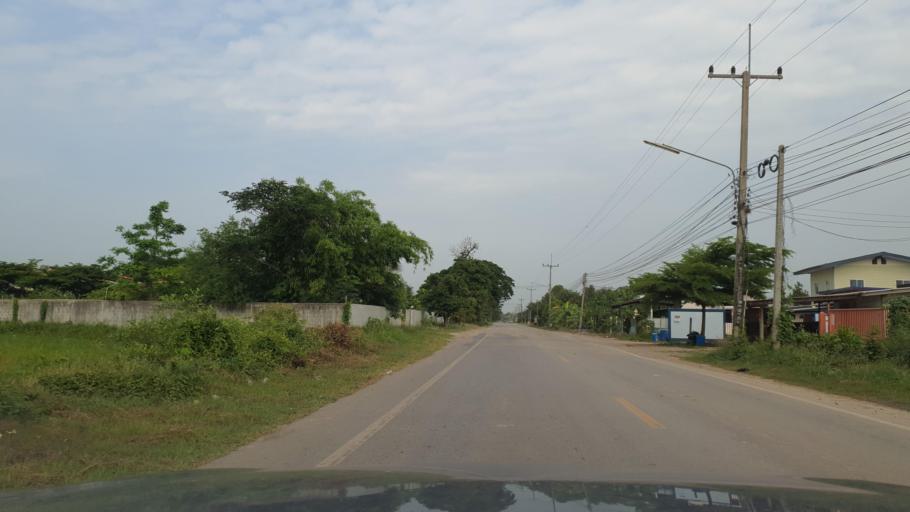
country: TH
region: Phitsanulok
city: Bang Rakam
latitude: 16.8147
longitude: 100.1765
